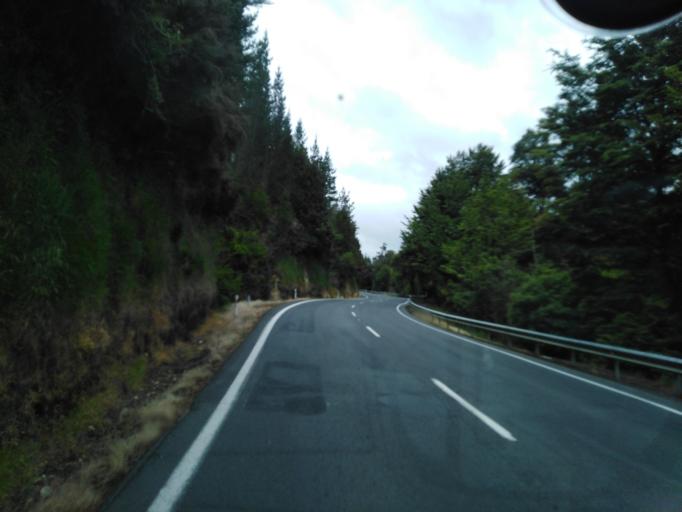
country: NZ
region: Tasman
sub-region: Tasman District
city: Wakefield
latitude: -41.6244
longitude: 172.7298
